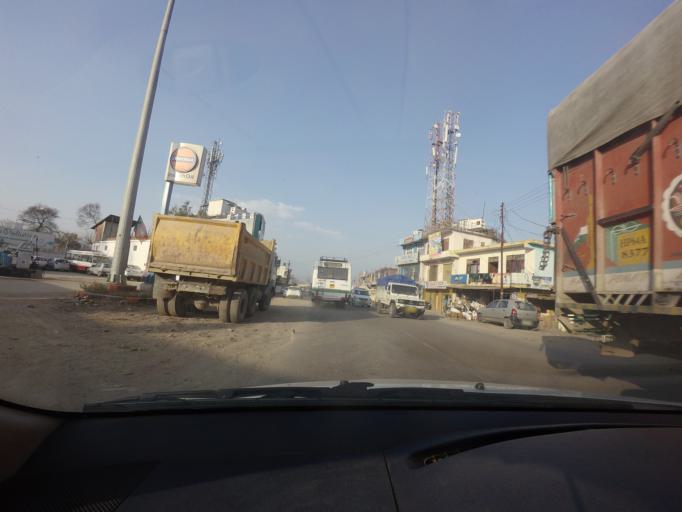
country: IN
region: Himachal Pradesh
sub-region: Mandi
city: Sundarnagar
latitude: 31.5531
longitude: 76.9009
